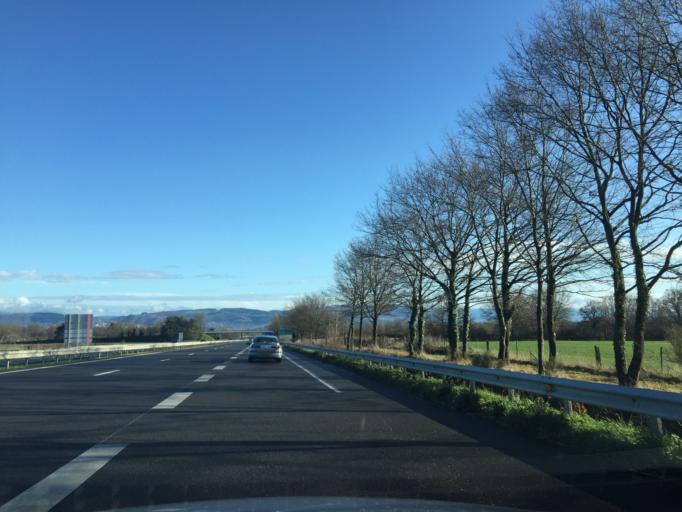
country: FR
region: Auvergne
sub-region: Departement du Puy-de-Dome
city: Orleat
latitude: 45.8509
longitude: 3.4125
